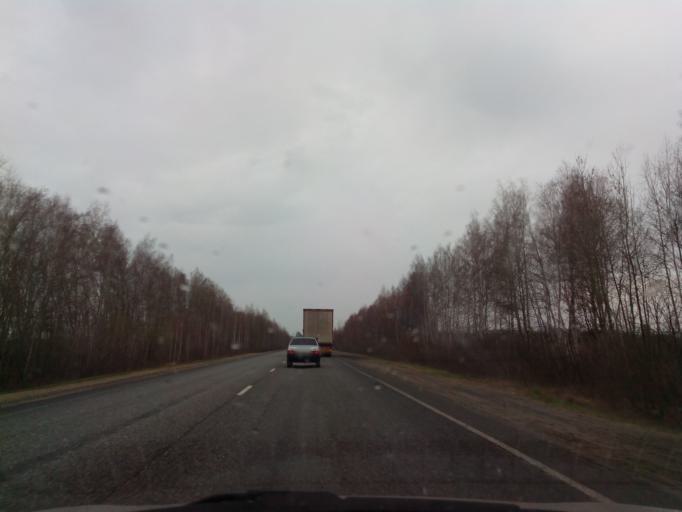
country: RU
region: Tambov
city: Pervomayskiy
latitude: 53.1256
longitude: 40.3855
